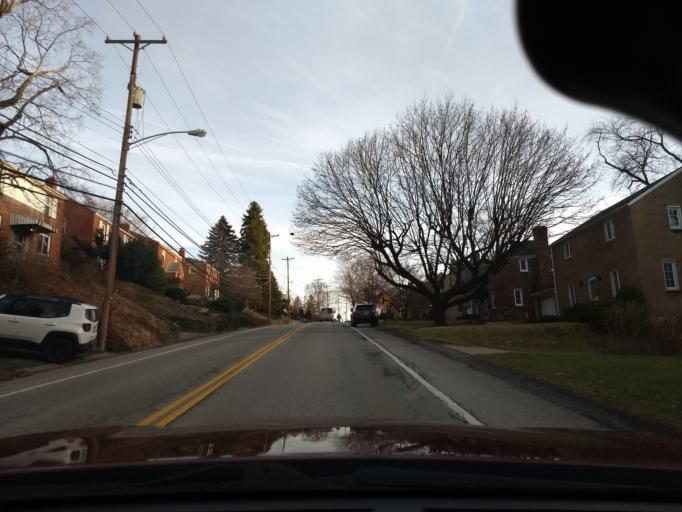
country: US
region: Pennsylvania
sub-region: Allegheny County
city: Brentwood
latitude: 40.3648
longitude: -79.9698
